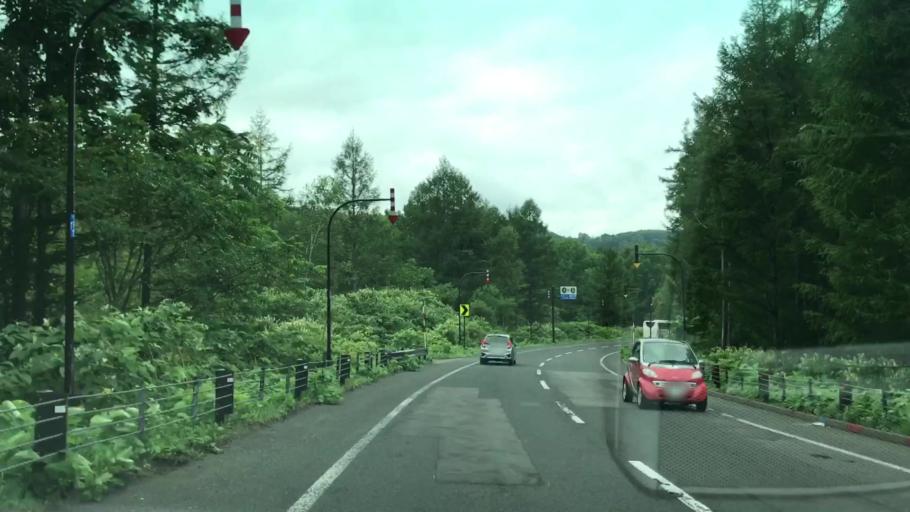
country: JP
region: Hokkaido
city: Niseko Town
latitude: 42.9491
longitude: 140.8522
